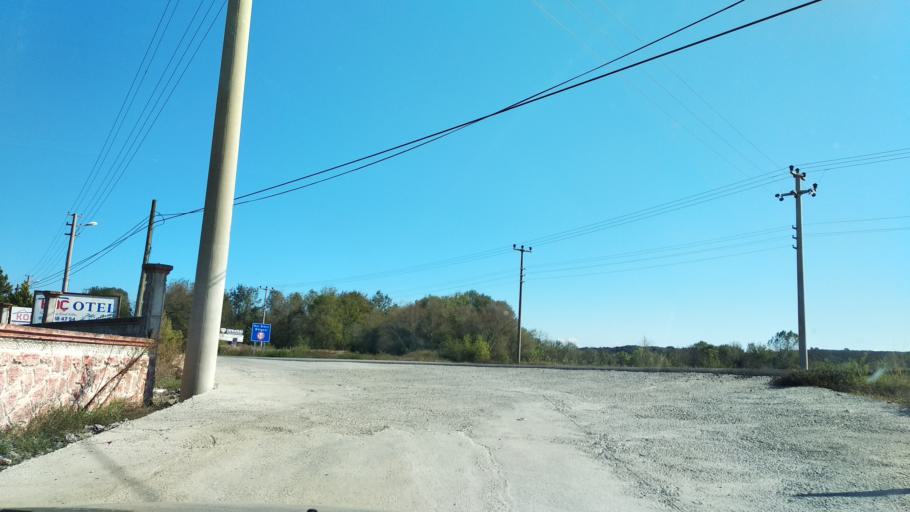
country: TR
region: Sakarya
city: Karasu
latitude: 41.1192
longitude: 30.6085
